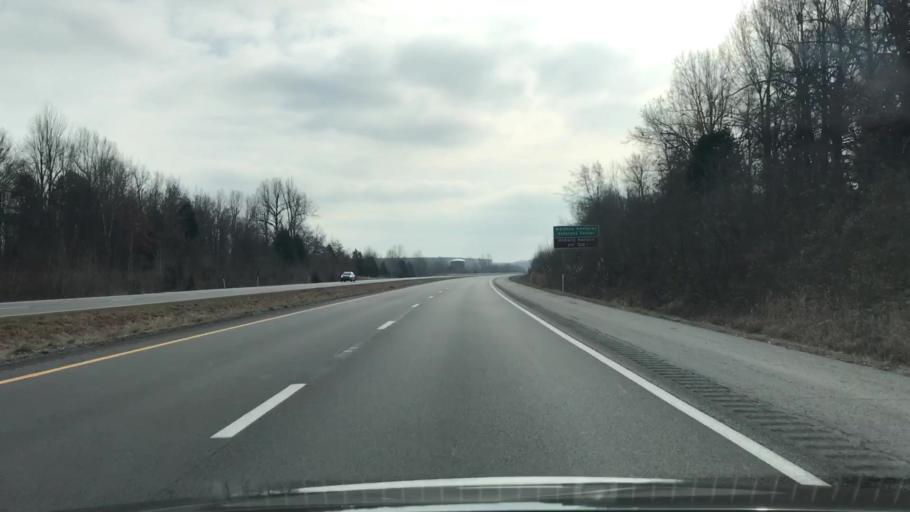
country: US
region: Kentucky
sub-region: Hopkins County
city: Madisonville
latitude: 37.4318
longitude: -87.4723
